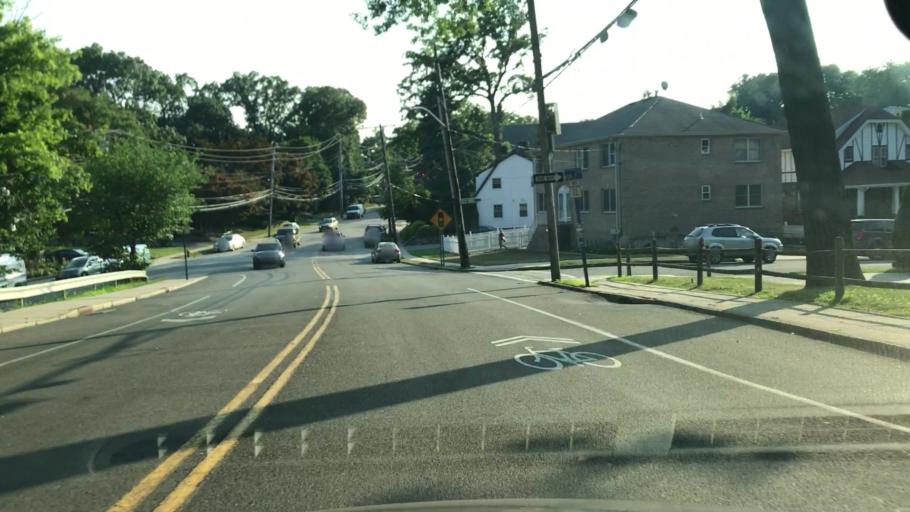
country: US
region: New York
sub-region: Westchester County
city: Bronxville
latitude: 40.9449
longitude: -73.8586
